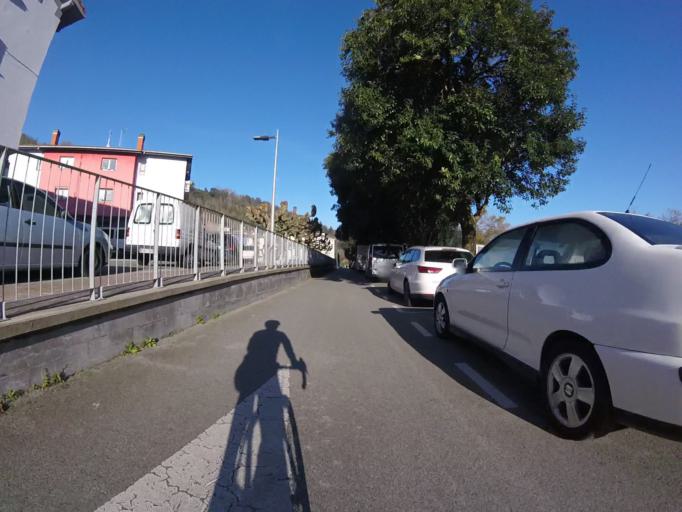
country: ES
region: Basque Country
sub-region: Provincia de Guipuzcoa
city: Usurbil
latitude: 43.2665
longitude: -2.0563
